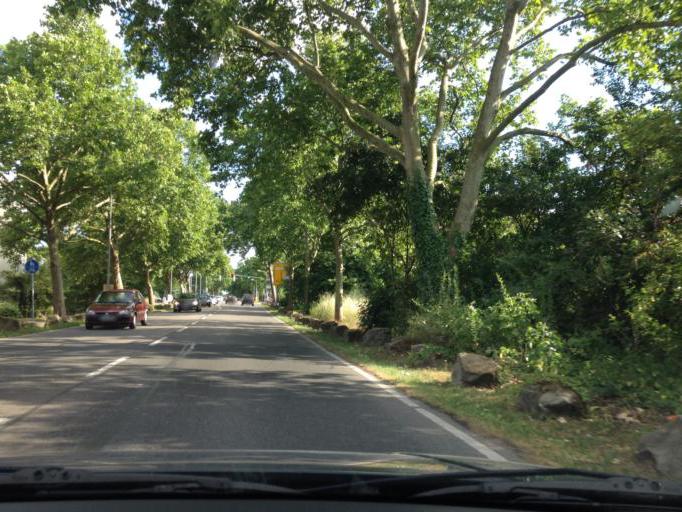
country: DE
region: Rheinland-Pfalz
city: Frankenthal
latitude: 49.5212
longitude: 8.3547
